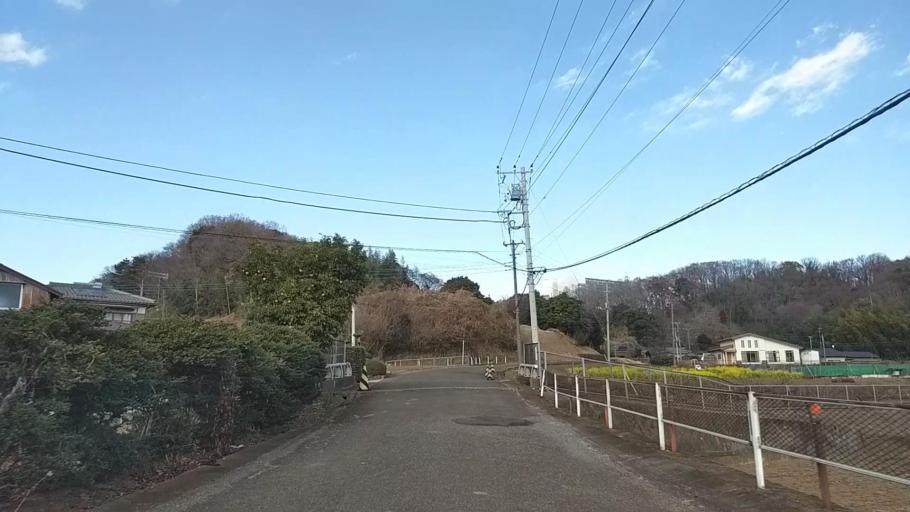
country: JP
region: Kanagawa
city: Isehara
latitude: 35.4159
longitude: 139.3167
